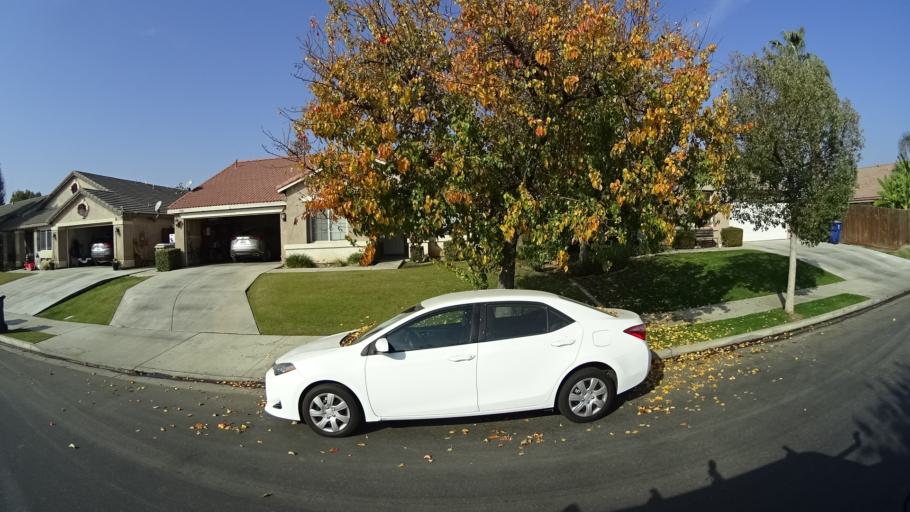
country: US
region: California
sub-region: Kern County
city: Greenacres
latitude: 35.4138
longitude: -119.1184
